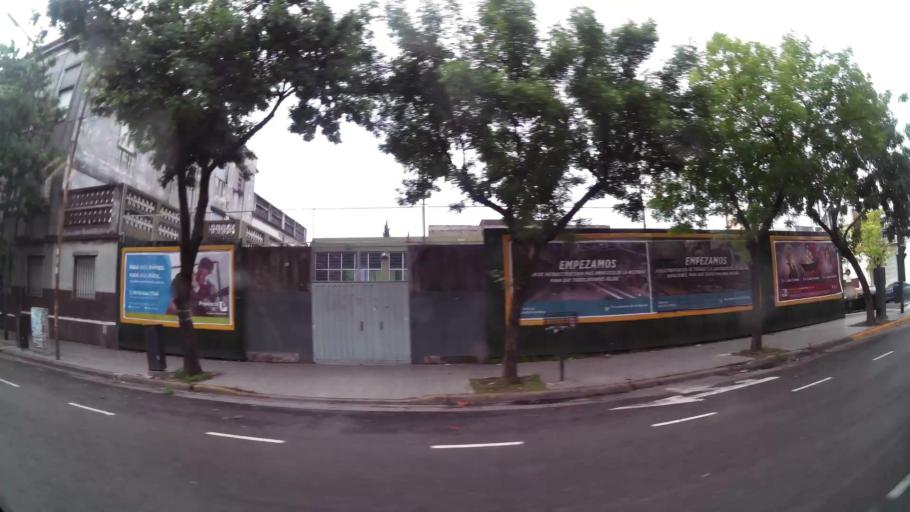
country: AR
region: Buenos Aires F.D.
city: Buenos Aires
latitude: -34.6323
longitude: -58.4246
